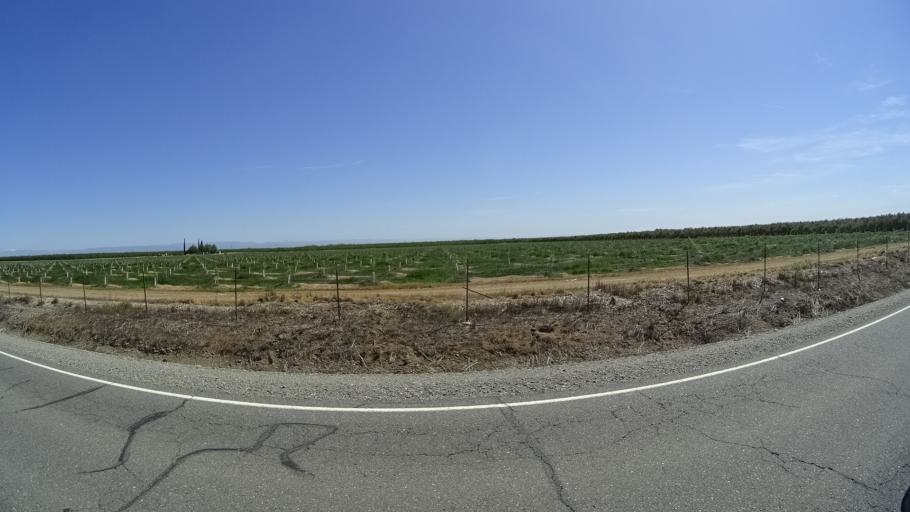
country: US
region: California
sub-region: Glenn County
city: Orland
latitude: 39.6899
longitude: -122.1402
